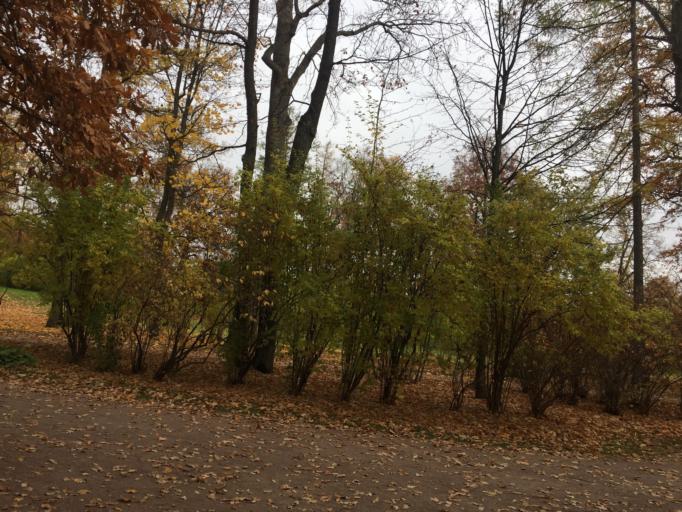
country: RU
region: St.-Petersburg
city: Pushkin
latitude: 59.7119
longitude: 30.3922
